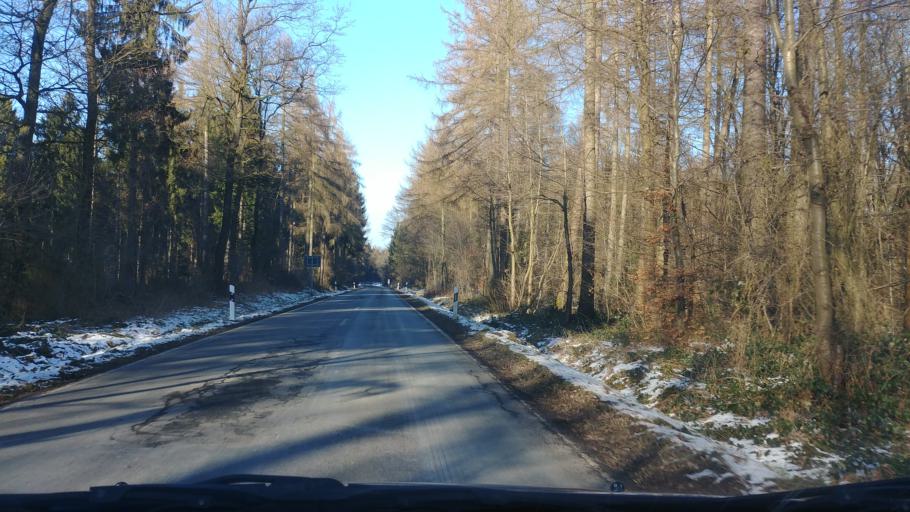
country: DE
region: Lower Saxony
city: Hardegsen
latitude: 51.7107
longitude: 9.7836
